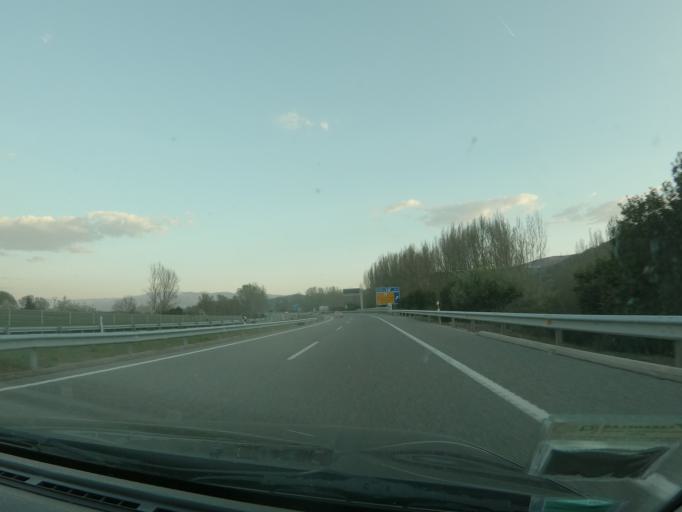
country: ES
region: Castille and Leon
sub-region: Provincia de Leon
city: Villafranca del Bierzo
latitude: 42.6021
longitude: -6.8177
